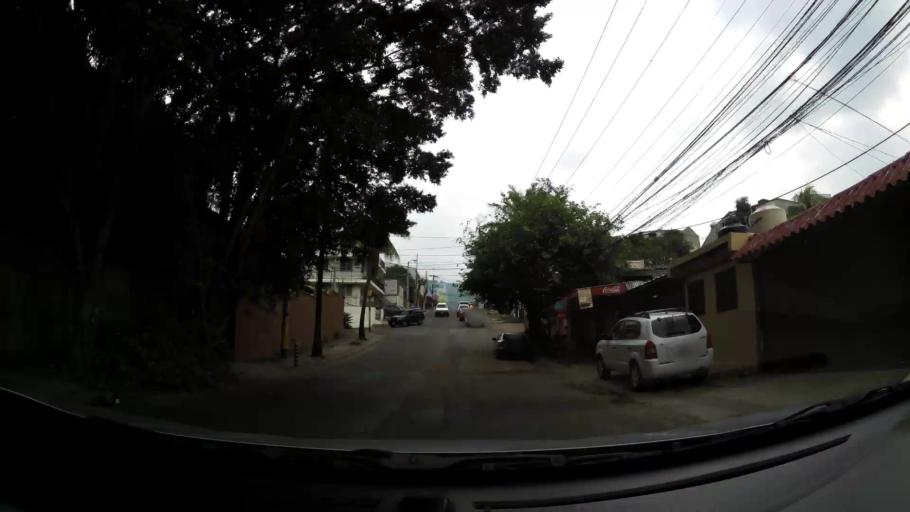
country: HN
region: Francisco Morazan
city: Tegucigalpa
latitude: 14.0985
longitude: -87.1913
